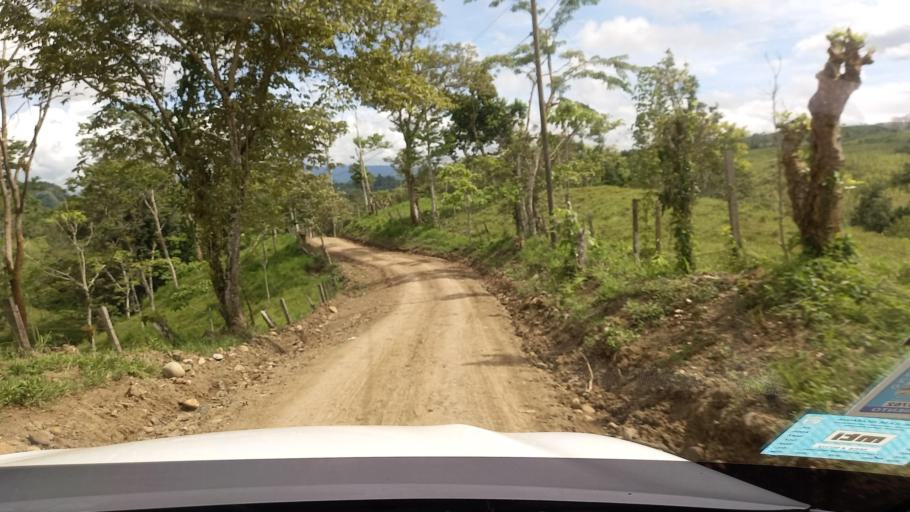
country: NI
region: Jinotega
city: San Jose de Bocay
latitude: 13.3781
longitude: -85.6852
